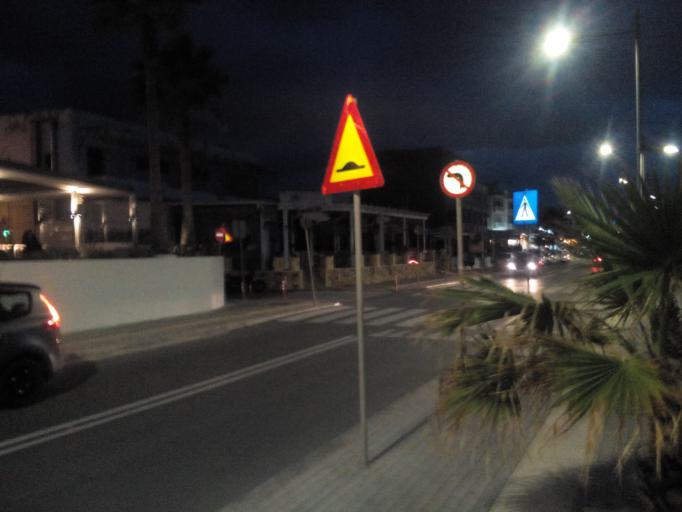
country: GR
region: Crete
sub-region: Nomos Rethymnis
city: Rethymno
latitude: 35.3675
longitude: 24.4981
